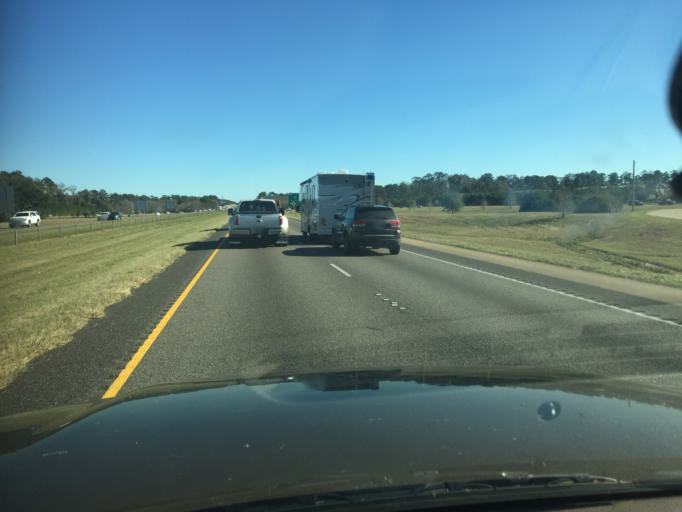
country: US
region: Louisiana
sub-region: Saint Tammany Parish
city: Covington
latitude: 30.4423
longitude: -90.1267
